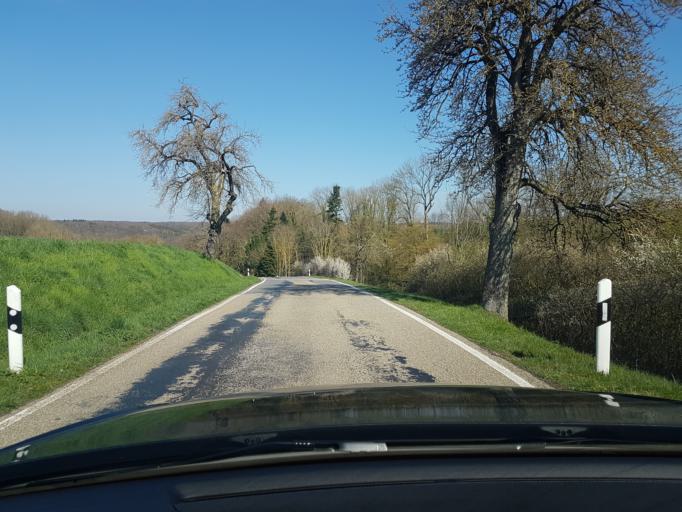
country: DE
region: Baden-Wuerttemberg
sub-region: Regierungsbezirk Stuttgart
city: Jagsthausen
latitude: 49.3231
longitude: 9.5122
